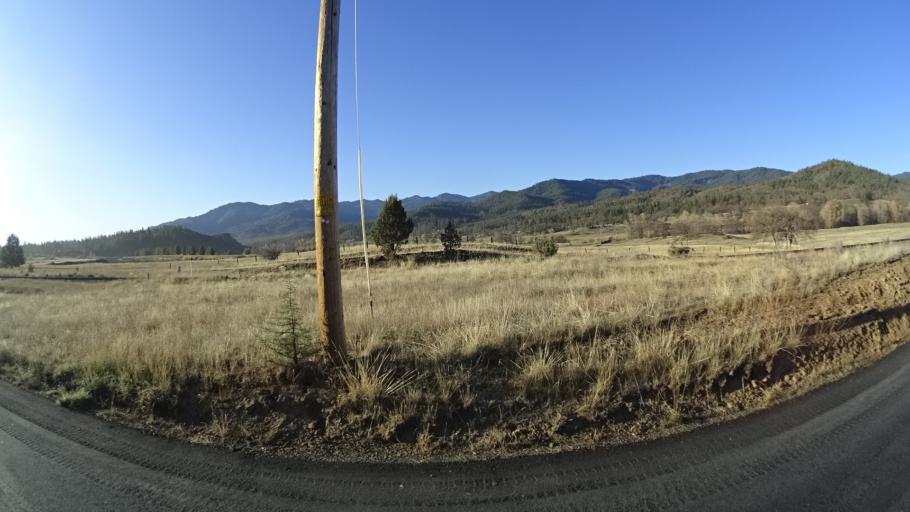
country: US
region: Oregon
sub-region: Jackson County
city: Ashland
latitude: 42.0004
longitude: -122.6360
